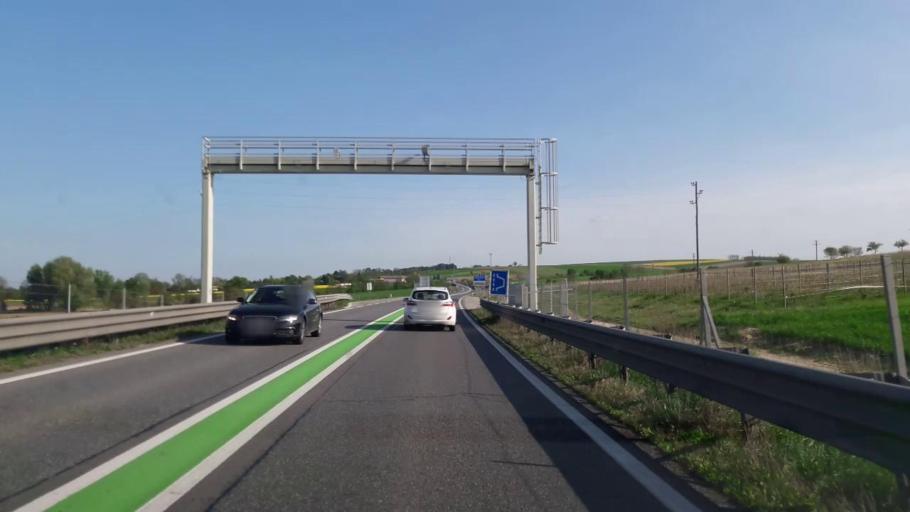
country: AT
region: Lower Austria
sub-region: Politischer Bezirk Hollabrunn
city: Gollersdorf
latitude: 48.4987
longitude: 16.1054
